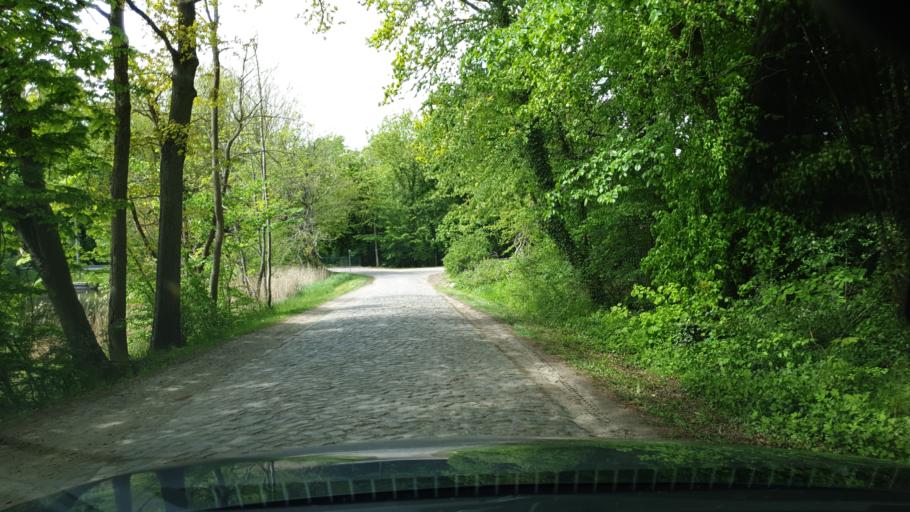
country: DE
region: Mecklenburg-Vorpommern
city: Bernitt
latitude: 53.9324
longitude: 11.8333
